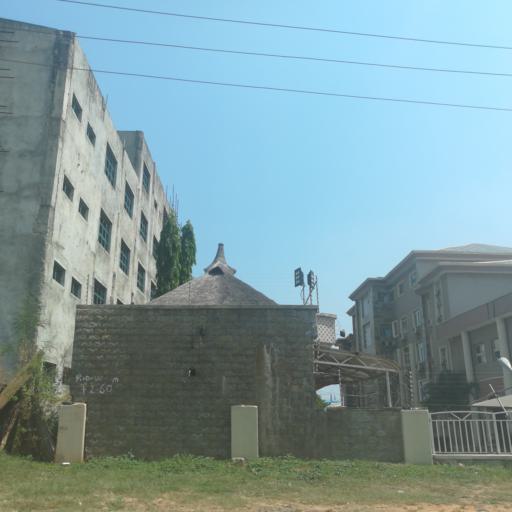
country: NG
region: Abuja Federal Capital Territory
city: Abuja
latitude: 9.0738
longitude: 7.4343
